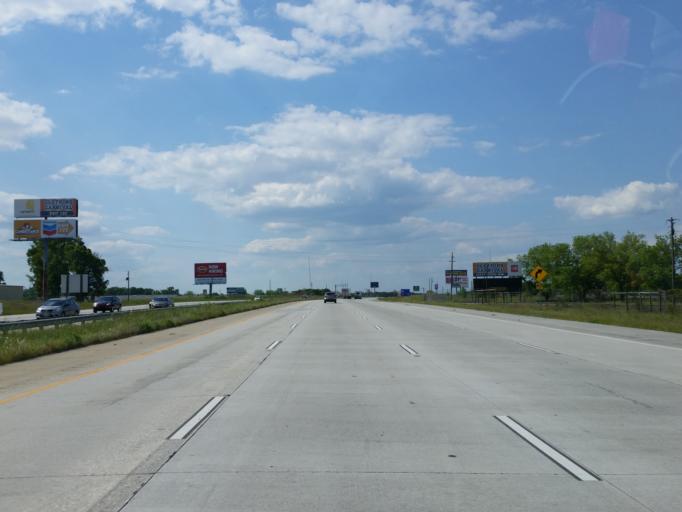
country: US
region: Georgia
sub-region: Dooly County
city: Unadilla
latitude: 32.2525
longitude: -83.7462
